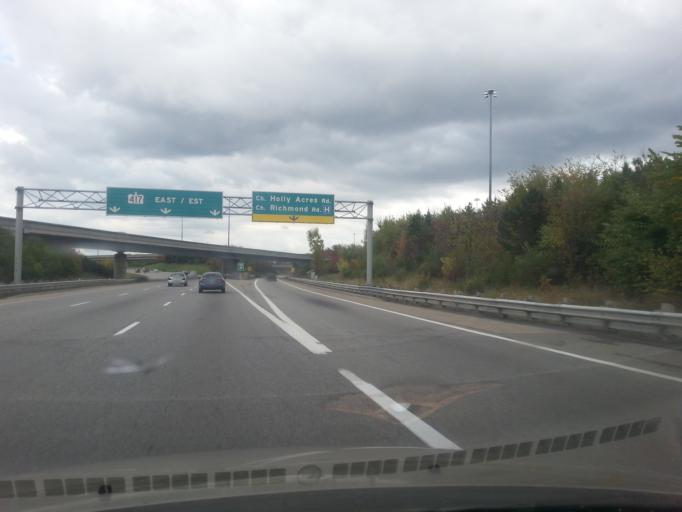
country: CA
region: Ontario
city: Bells Corners
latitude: 45.3425
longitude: -75.8202
